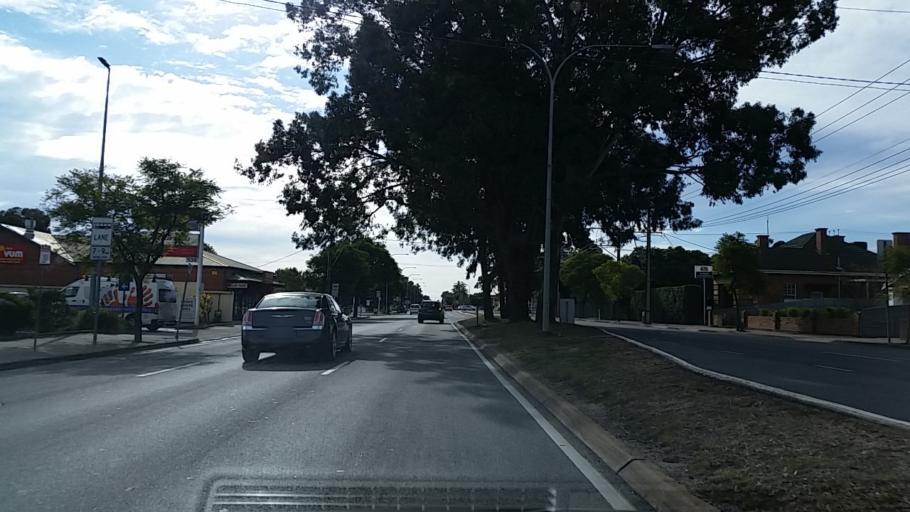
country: AU
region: South Australia
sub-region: Mitcham
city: Clarence Gardens
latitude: -34.9793
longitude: 138.5918
